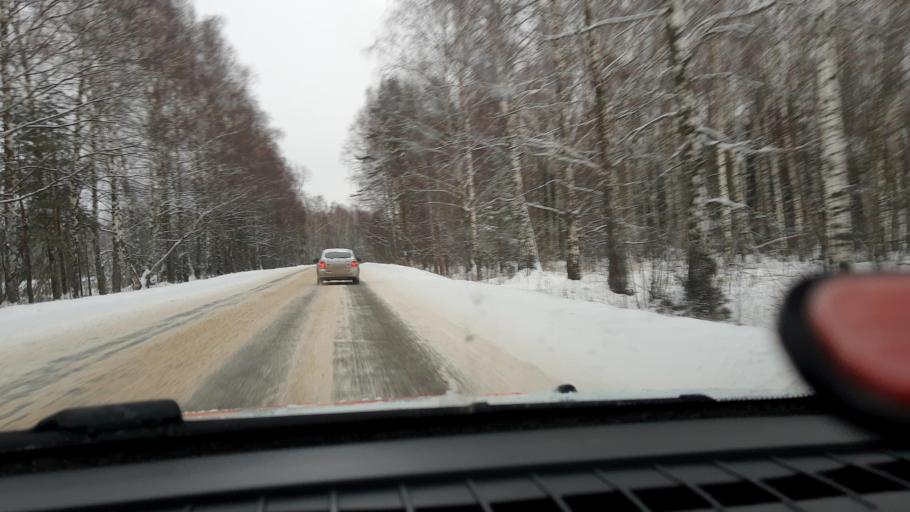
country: RU
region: Nizjnij Novgorod
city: Pamyat' Parizhskoy Kommuny
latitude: 56.2565
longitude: 44.4639
